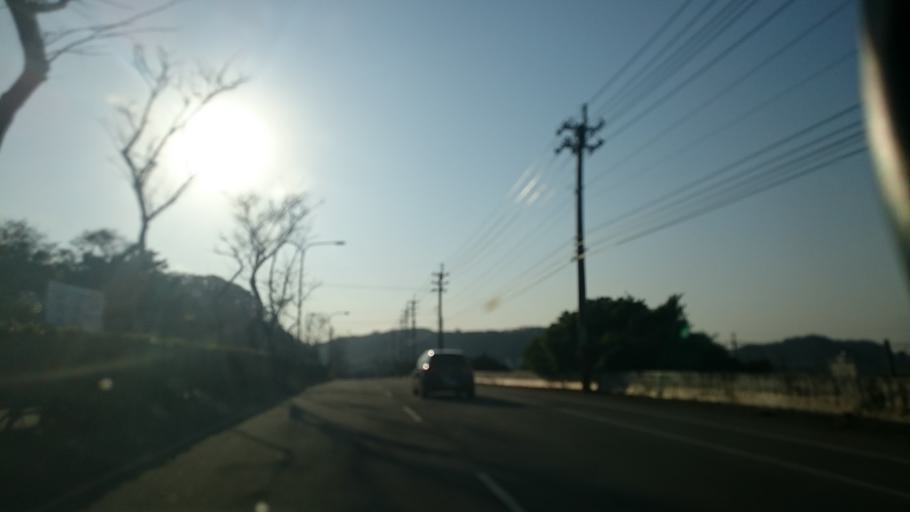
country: TW
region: Taiwan
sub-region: Miaoli
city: Miaoli
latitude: 24.6559
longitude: 120.8571
